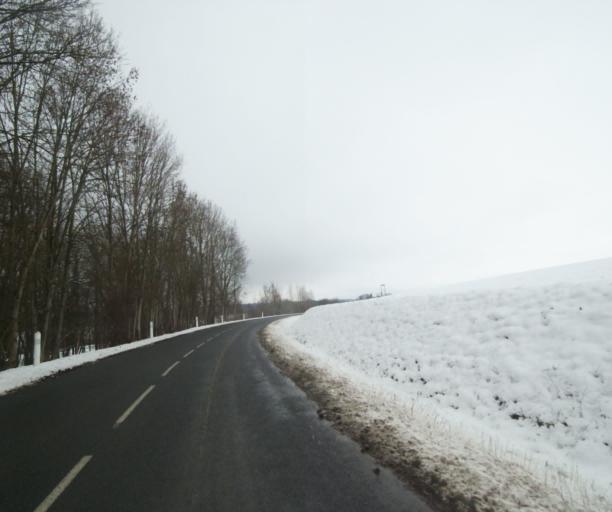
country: FR
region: Champagne-Ardenne
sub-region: Departement de la Haute-Marne
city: Wassy
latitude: 48.4415
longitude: 4.9557
